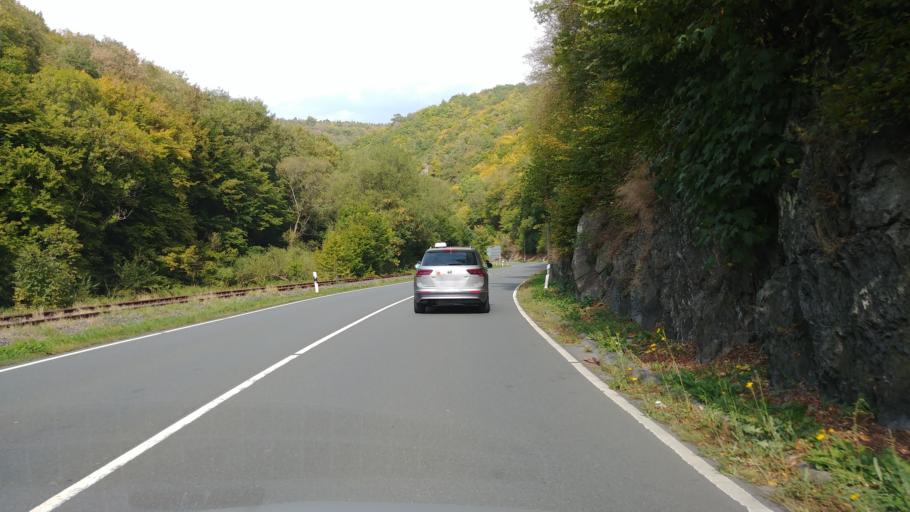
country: DE
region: Hesse
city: Burg Hohenstein
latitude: 50.1907
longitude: 8.0625
